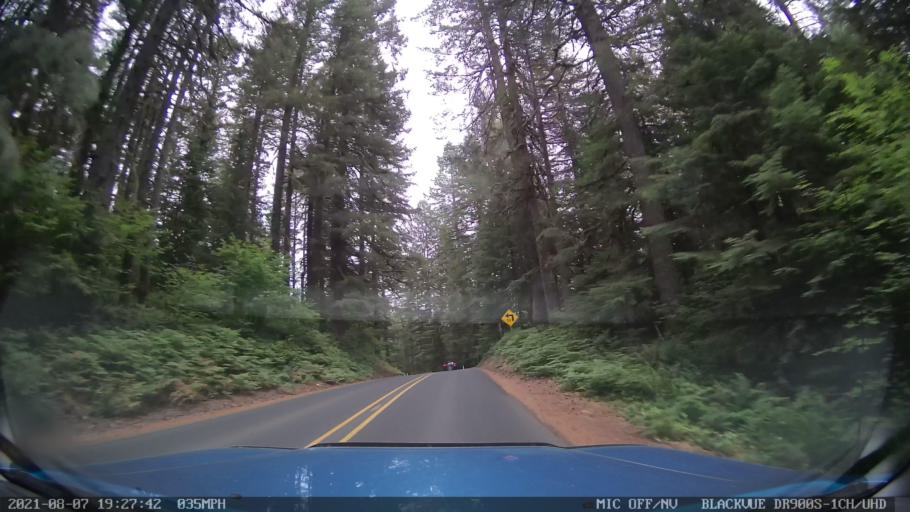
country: US
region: Oregon
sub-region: Linn County
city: Lyons
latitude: 44.8791
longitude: -122.6431
